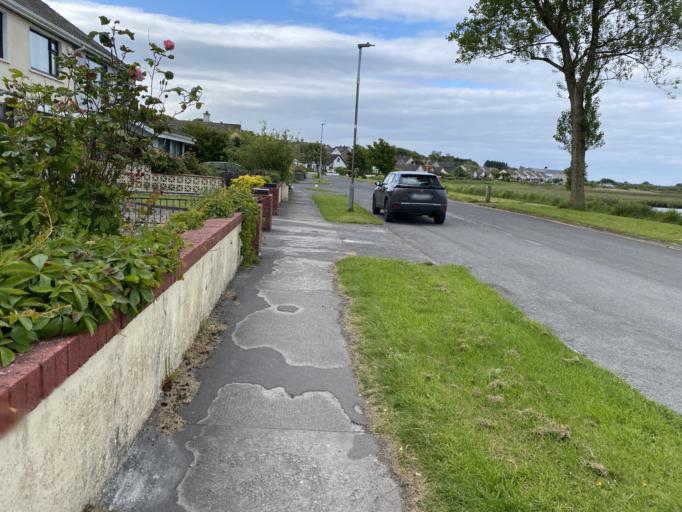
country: IE
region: Connaught
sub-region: County Galway
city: Gaillimh
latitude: 53.2783
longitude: -9.0292
